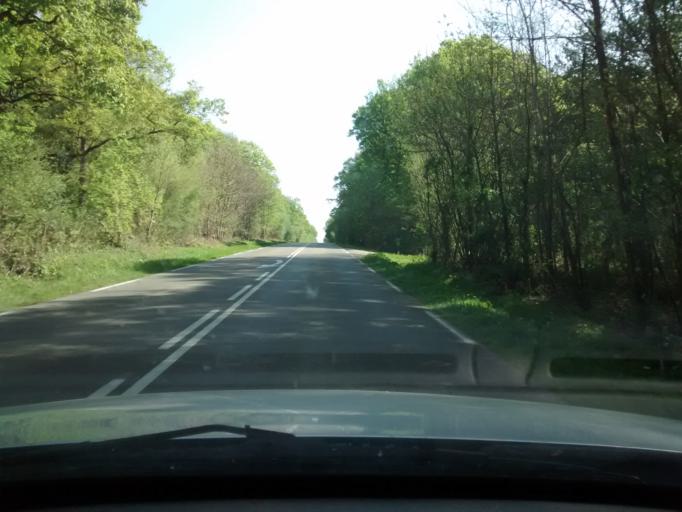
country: FR
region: Pays de la Loire
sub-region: Departement de la Mayenne
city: Montsurs
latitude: 48.1063
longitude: -0.4997
